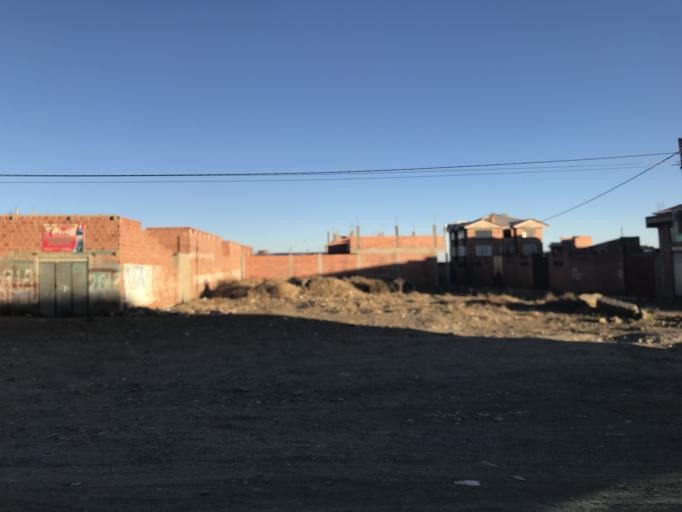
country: BO
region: La Paz
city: La Paz
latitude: -16.5060
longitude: -68.2552
